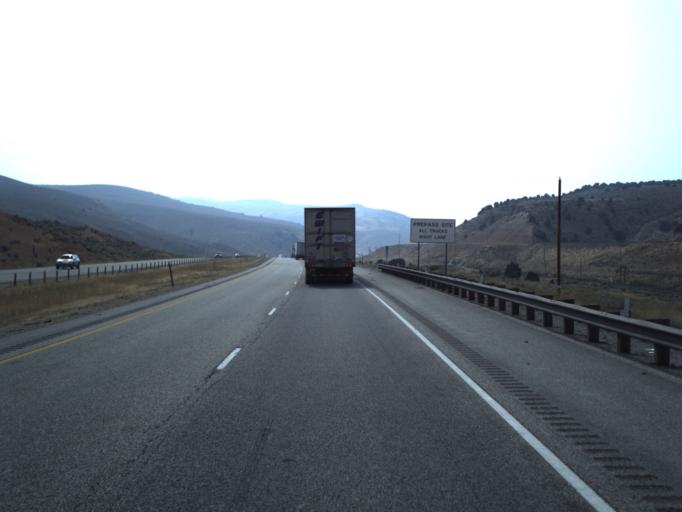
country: US
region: Utah
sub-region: Summit County
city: Coalville
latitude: 41.0976
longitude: -111.2180
